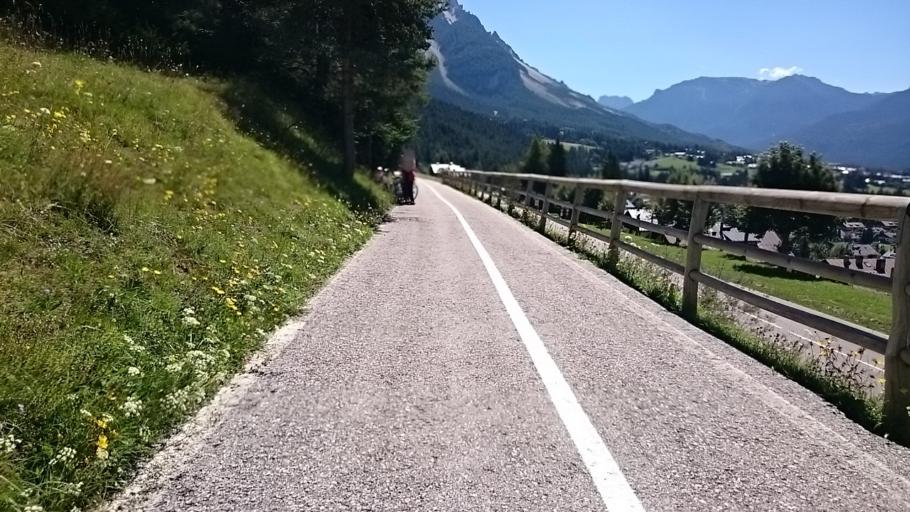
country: IT
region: Veneto
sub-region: Provincia di Belluno
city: San Vito
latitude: 46.4777
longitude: 12.1983
